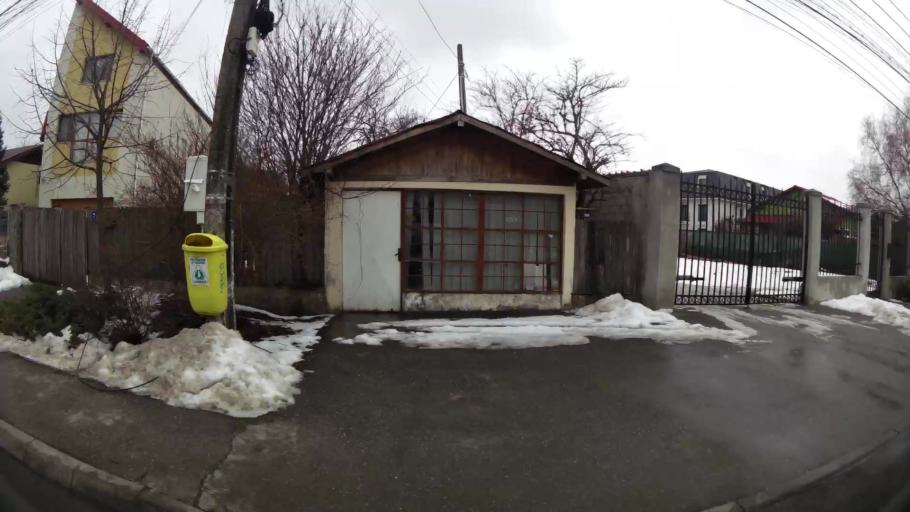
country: RO
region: Ilfov
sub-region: Comuna Otopeni
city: Otopeni
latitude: 44.5525
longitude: 26.0800
